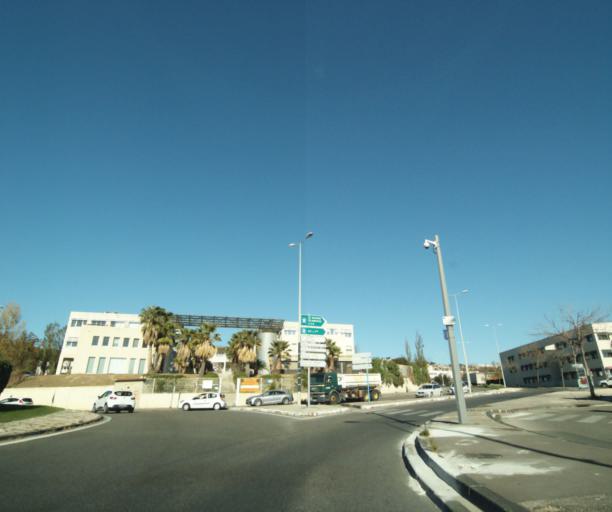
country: FR
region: Provence-Alpes-Cote d'Azur
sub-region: Departement des Bouches-du-Rhone
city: Marseille 16
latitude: 43.3530
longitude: 5.3376
